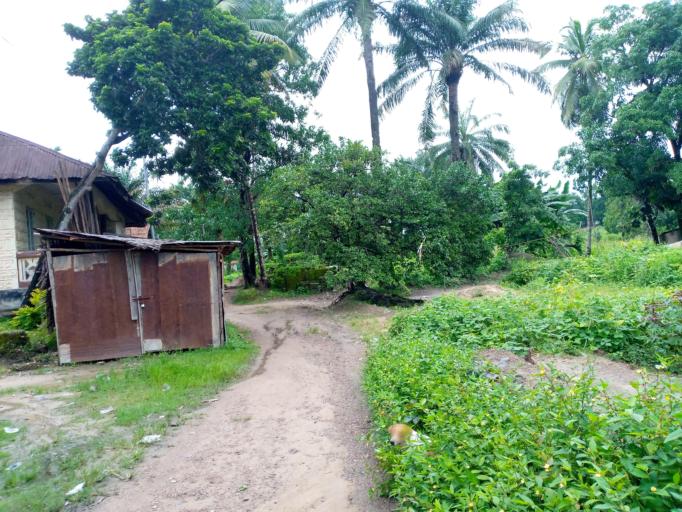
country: SL
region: Northern Province
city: Magburaka
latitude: 8.7214
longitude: -11.9464
